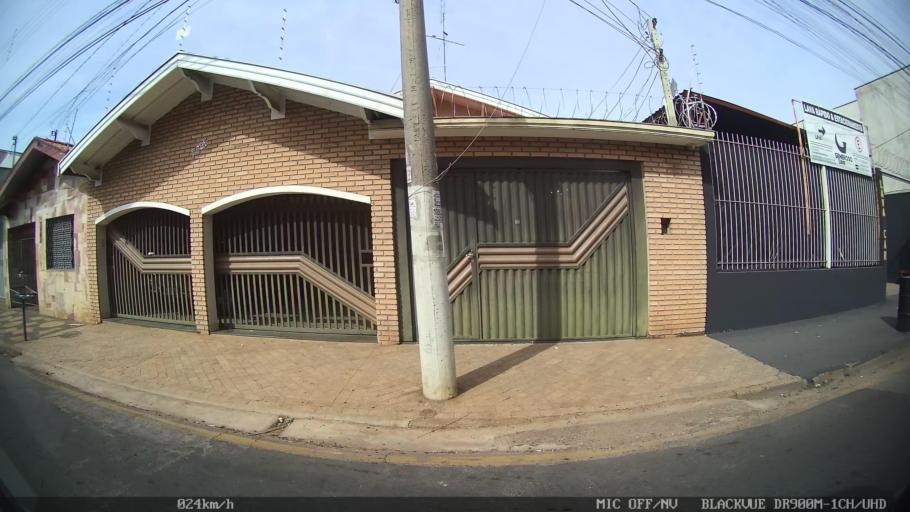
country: BR
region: Sao Paulo
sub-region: Piracicaba
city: Piracicaba
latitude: -22.7411
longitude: -47.6533
